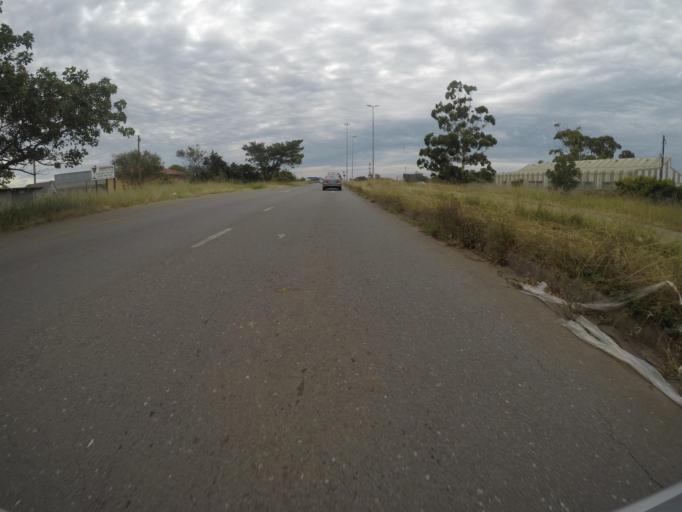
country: ZA
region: Eastern Cape
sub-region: Buffalo City Metropolitan Municipality
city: East London
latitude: -32.9720
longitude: 27.8514
